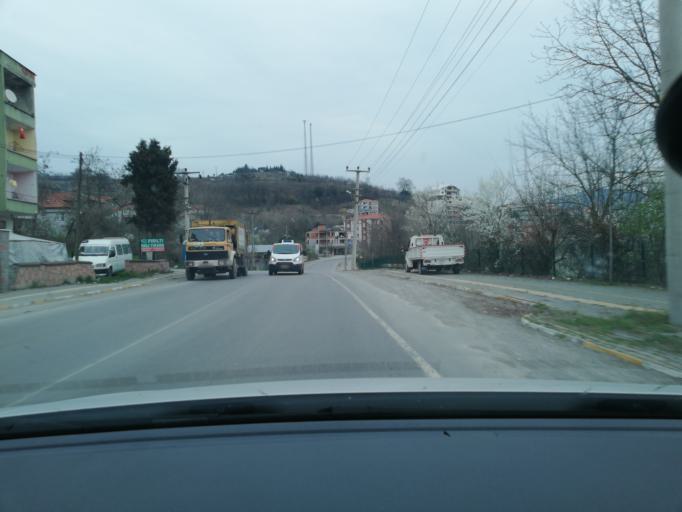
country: TR
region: Zonguldak
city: Gokcebey
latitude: 41.3093
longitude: 32.1293
